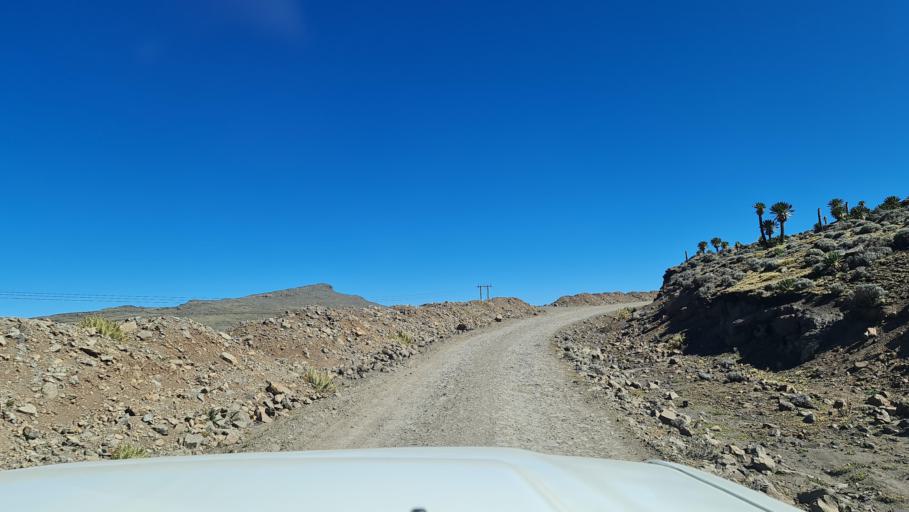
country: ET
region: Amhara
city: Debark'
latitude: 13.2117
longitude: 38.2122
